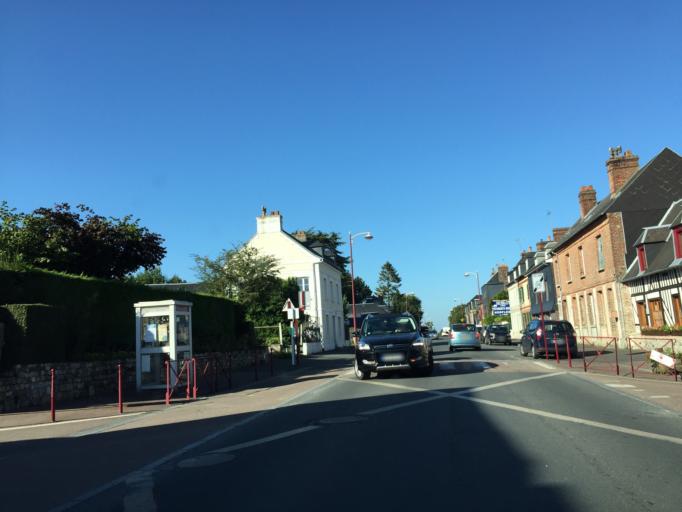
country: FR
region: Lower Normandy
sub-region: Departement du Calvados
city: Equemauville
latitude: 49.3928
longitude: 0.2081
